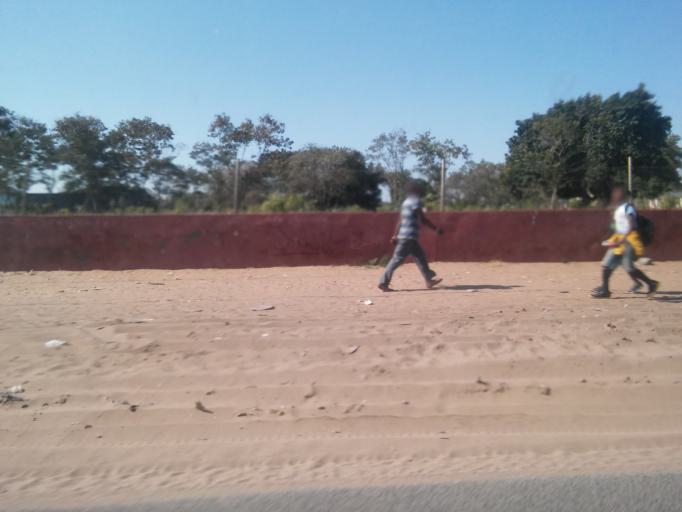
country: MZ
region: Maputo City
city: Maputo
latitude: -25.8578
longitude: 32.5670
